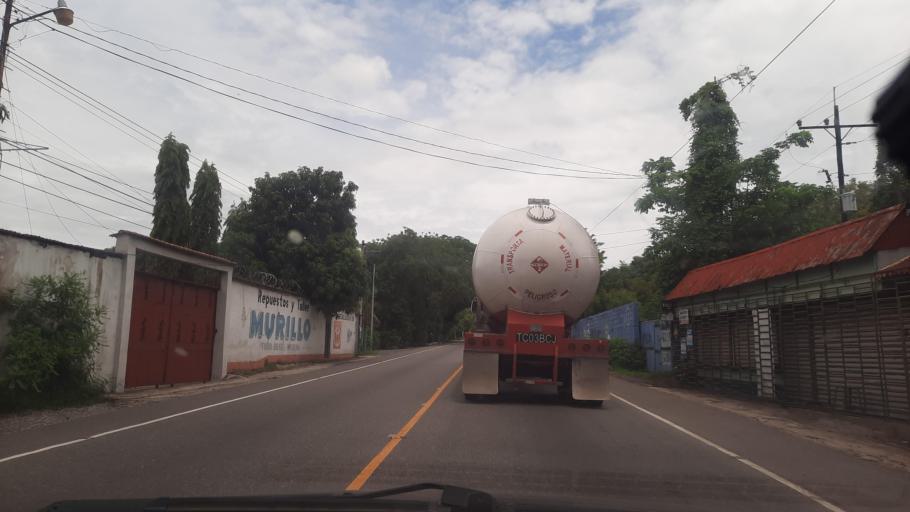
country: GT
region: Zacapa
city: Rio Hondo
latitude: 15.0696
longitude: -89.5142
